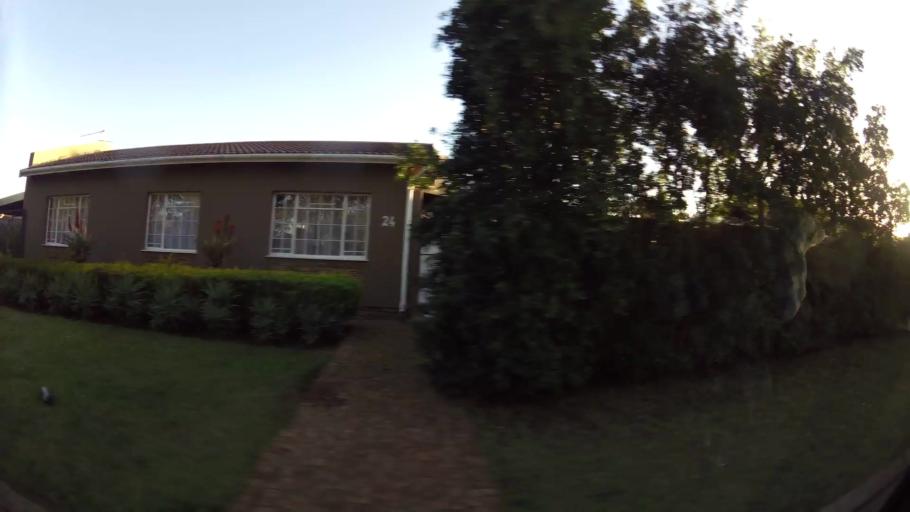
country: ZA
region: Western Cape
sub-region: Eden District Municipality
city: Riversdale
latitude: -34.0820
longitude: 21.2479
